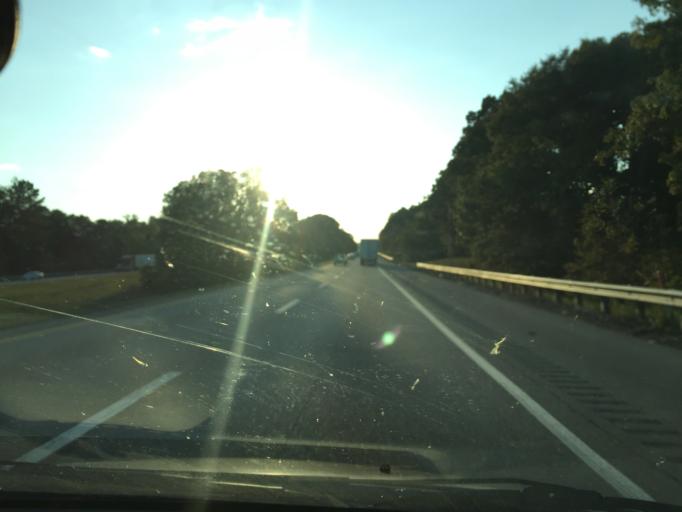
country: US
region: Tennessee
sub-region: Bradley County
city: Cleveland
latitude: 35.1469
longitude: -84.9667
